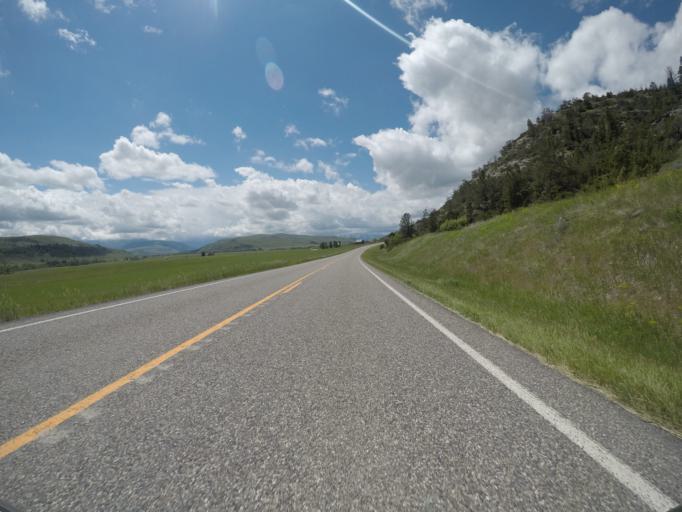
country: US
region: Montana
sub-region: Sweet Grass County
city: Big Timber
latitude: 45.6717
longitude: -110.0954
